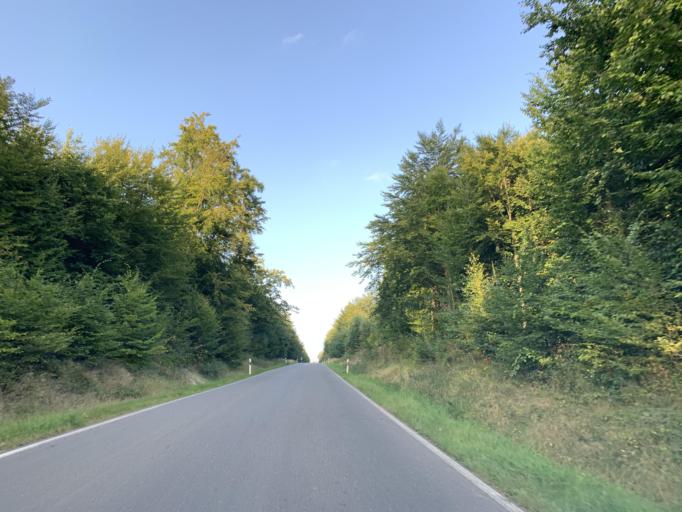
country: DE
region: Mecklenburg-Vorpommern
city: Loitz
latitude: 53.3540
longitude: 13.4293
